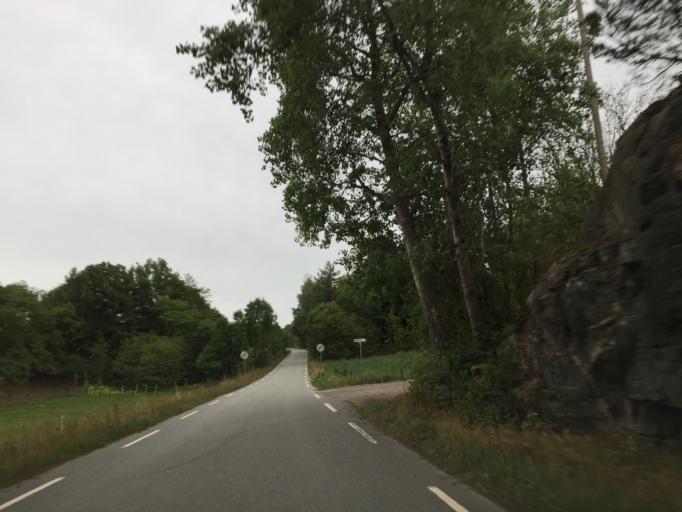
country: NO
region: Ostfold
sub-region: Hvaler
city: Skjaerhalden
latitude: 59.0736
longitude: 11.0051
